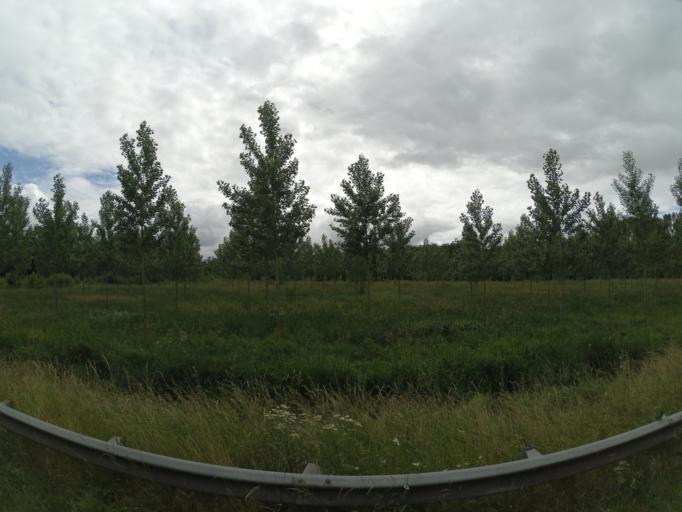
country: FR
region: Aquitaine
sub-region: Departement de la Gironde
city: Soussans
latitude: 45.0634
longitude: -0.7188
